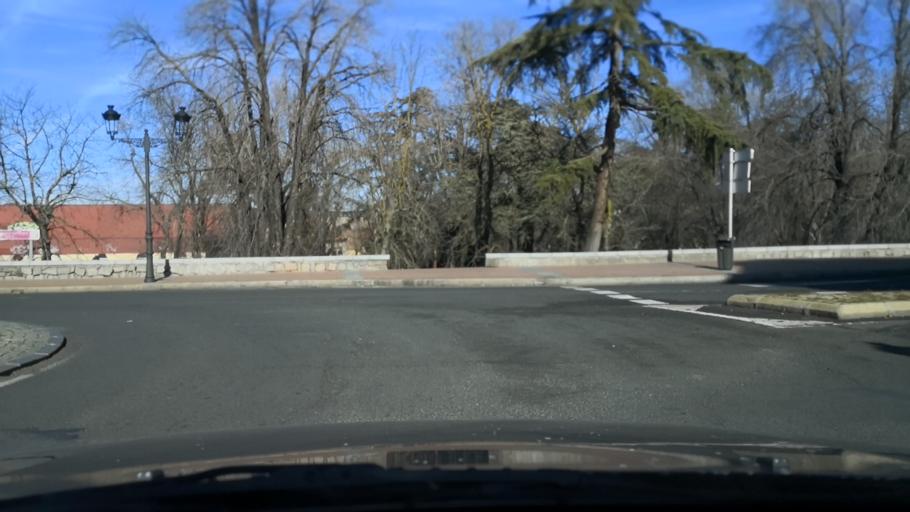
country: ES
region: Castille and Leon
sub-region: Provincia de Avila
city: Avila
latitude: 40.6569
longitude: -4.6883
